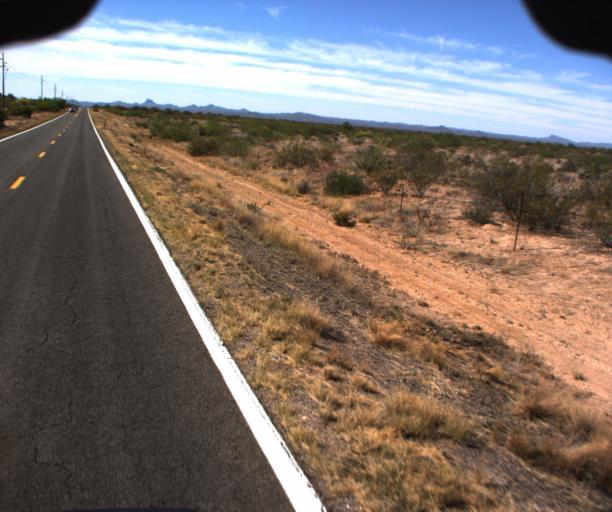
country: US
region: Arizona
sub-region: Yavapai County
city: Congress
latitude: 34.1256
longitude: -112.8375
